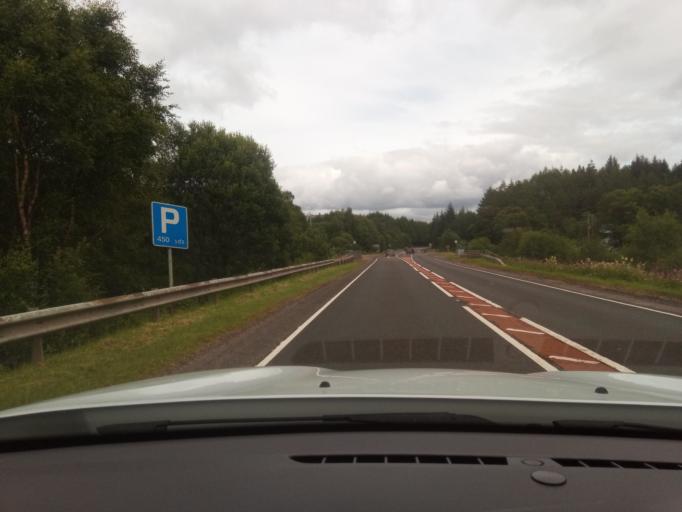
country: GB
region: Scotland
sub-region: Stirling
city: Callander
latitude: 56.3534
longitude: -4.3269
